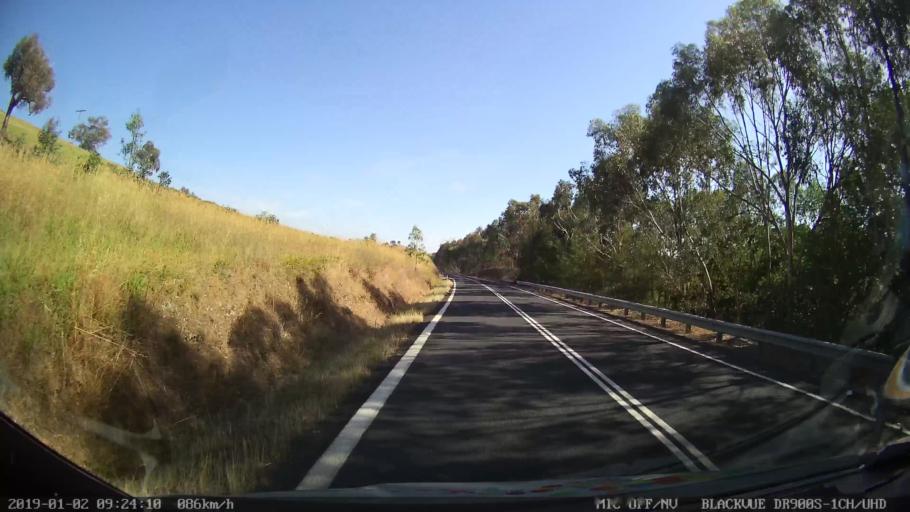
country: AU
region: New South Wales
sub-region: Tumut Shire
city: Tumut
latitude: -35.3806
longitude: 148.2918
